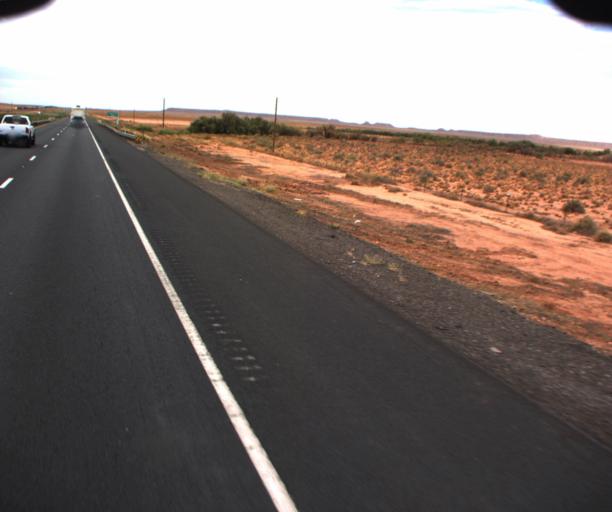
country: US
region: Arizona
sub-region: Coconino County
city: LeChee
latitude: 35.0496
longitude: -110.7739
